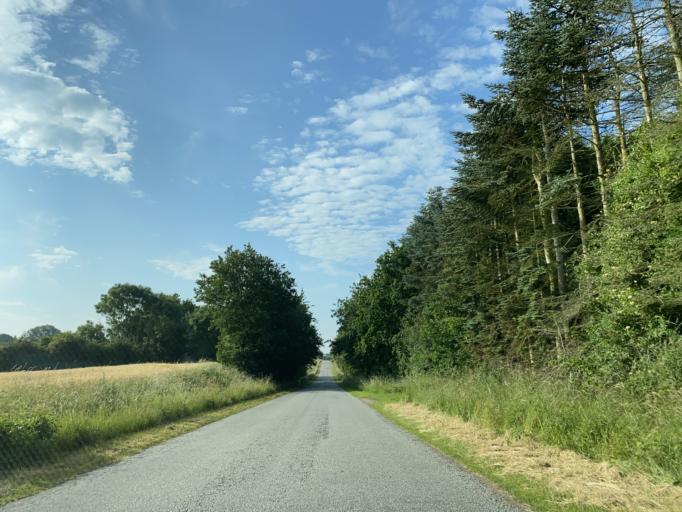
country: DK
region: South Denmark
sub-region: Haderslev Kommune
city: Haderslev
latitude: 55.1846
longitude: 9.4784
